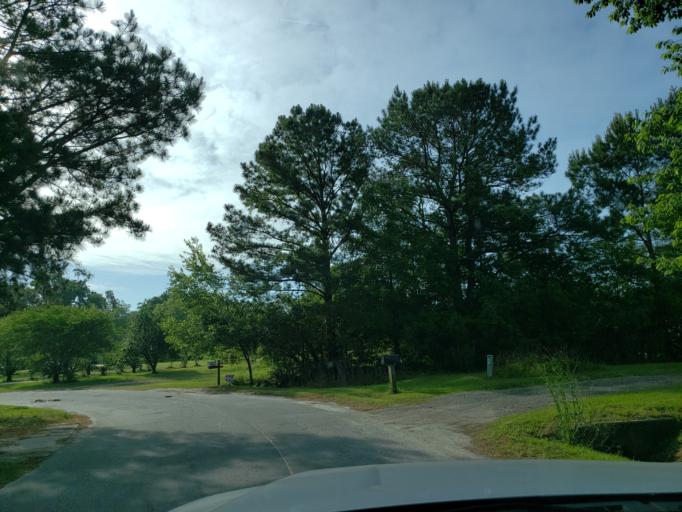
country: US
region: Georgia
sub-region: Chatham County
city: Georgetown
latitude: 32.0031
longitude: -81.2276
